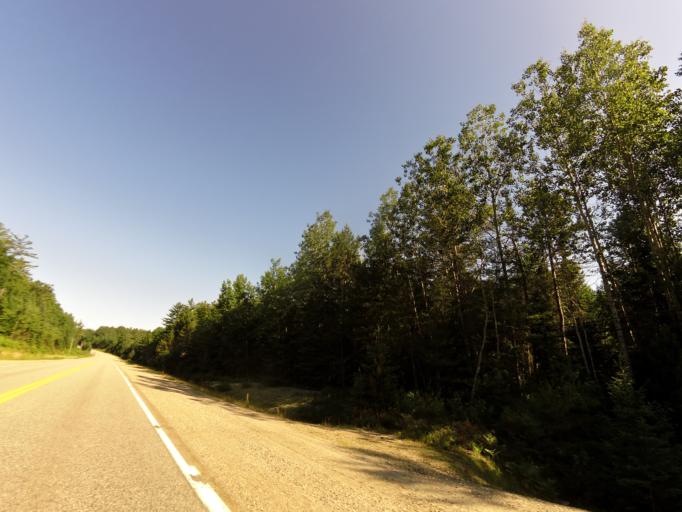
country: CA
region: Ontario
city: Deep River
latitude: 46.1754
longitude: -77.6475
